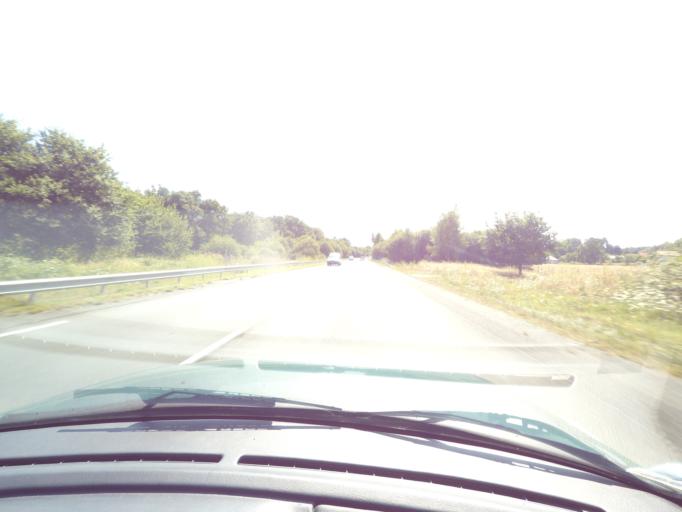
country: FR
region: Limousin
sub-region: Departement de la Haute-Vienne
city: Chaptelat
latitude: 45.8978
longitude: 1.2421
